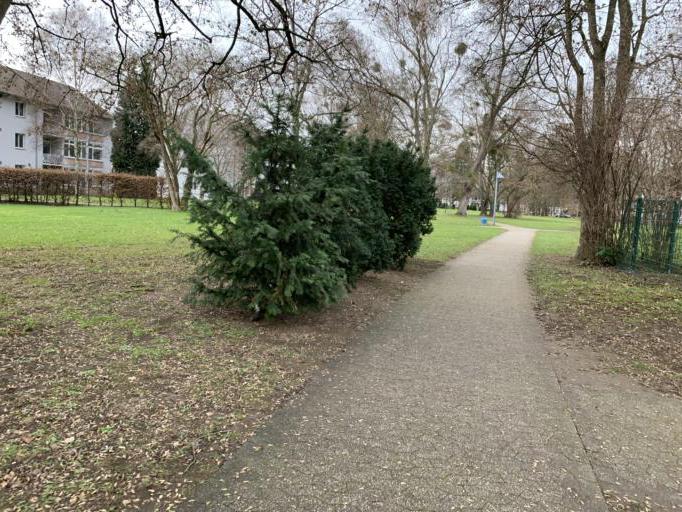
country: DE
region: North Rhine-Westphalia
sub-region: Regierungsbezirk Koln
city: Konigswinter
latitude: 50.7045
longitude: 7.1564
